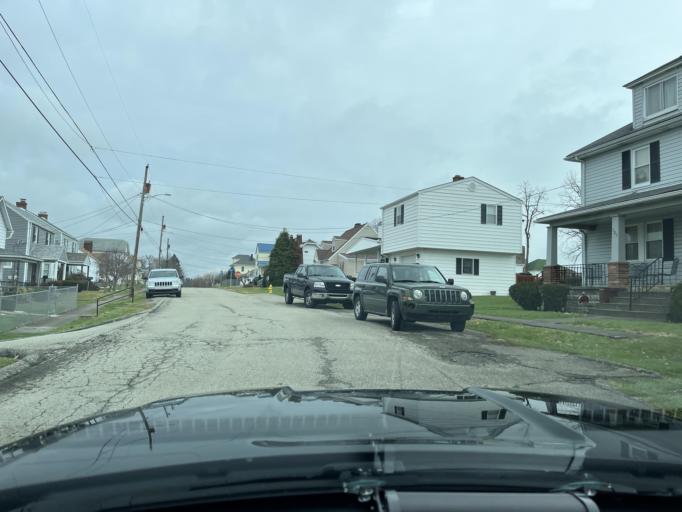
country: US
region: Pennsylvania
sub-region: Fayette County
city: South Uniontown
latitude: 39.8924
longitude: -79.7495
